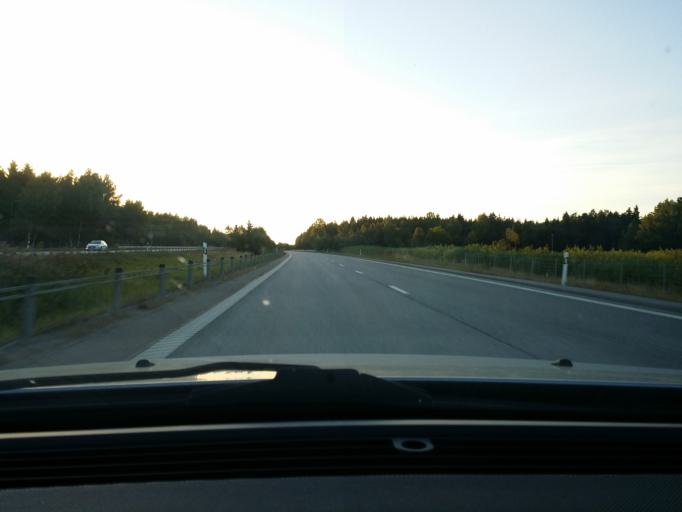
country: SE
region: Stockholm
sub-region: Upplands-Bro Kommun
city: Bro
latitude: 59.5400
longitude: 17.6151
